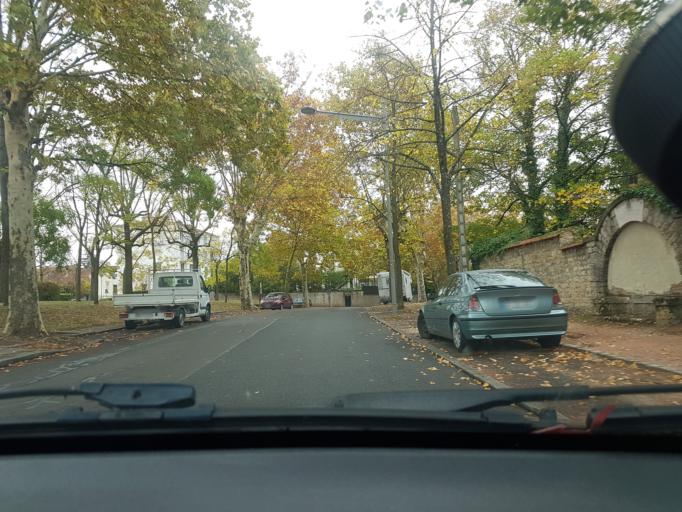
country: FR
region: Bourgogne
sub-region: Departement de la Cote-d'Or
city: Saint-Apollinaire
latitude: 47.3191
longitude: 5.0580
